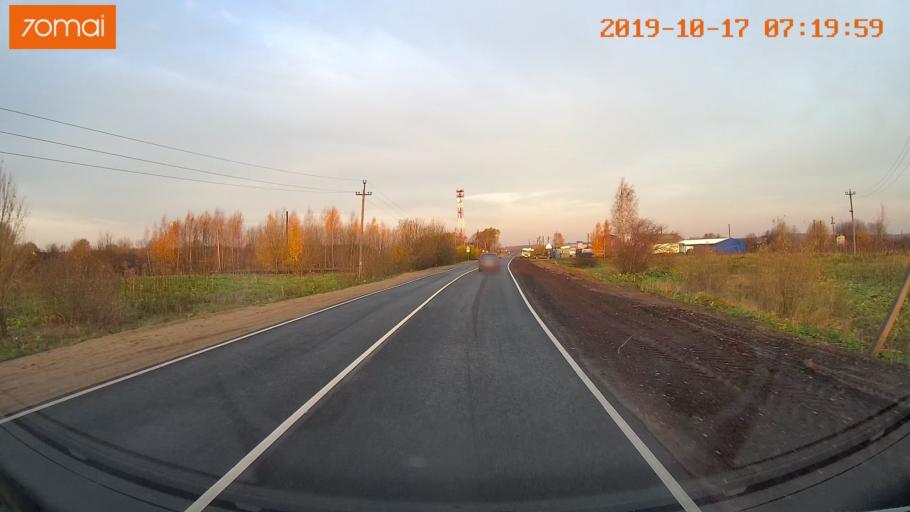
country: RU
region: Ivanovo
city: Gavrilov Posad
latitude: 56.3445
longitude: 40.1896
